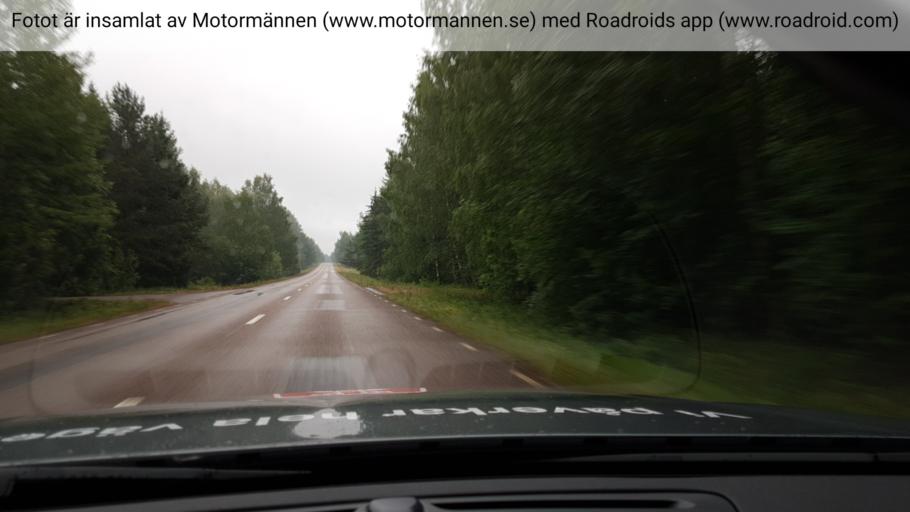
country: SE
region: Dalarna
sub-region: Avesta Kommun
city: Avesta
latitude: 59.9708
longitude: 16.1624
